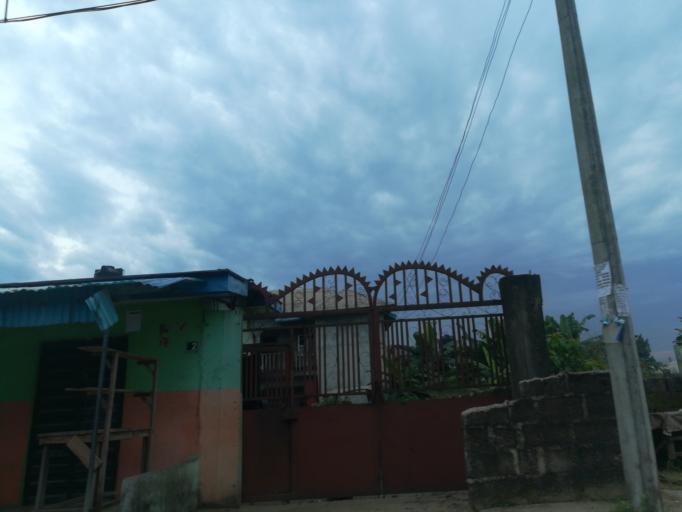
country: NG
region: Rivers
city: Port Harcourt
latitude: 4.8003
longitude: 6.9528
